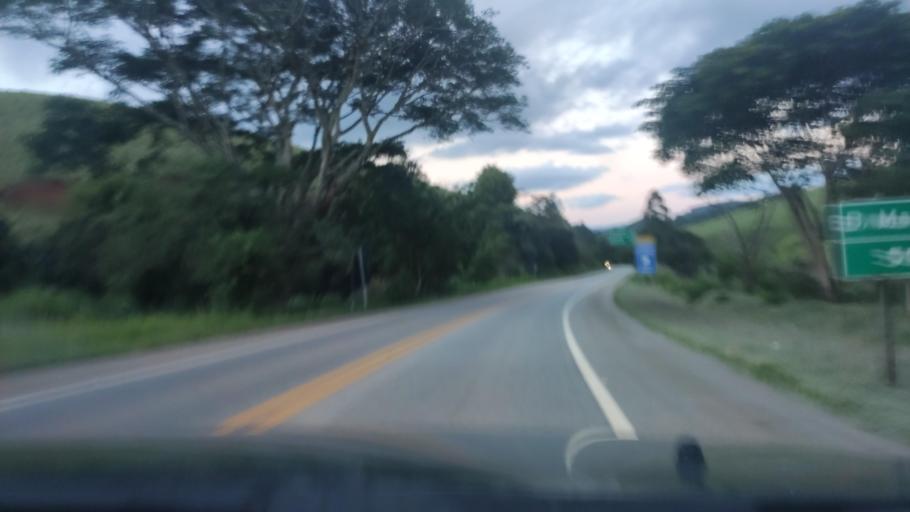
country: BR
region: Sao Paulo
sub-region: Campos Do Jordao
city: Campos do Jordao
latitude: -22.8098
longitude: -45.7533
